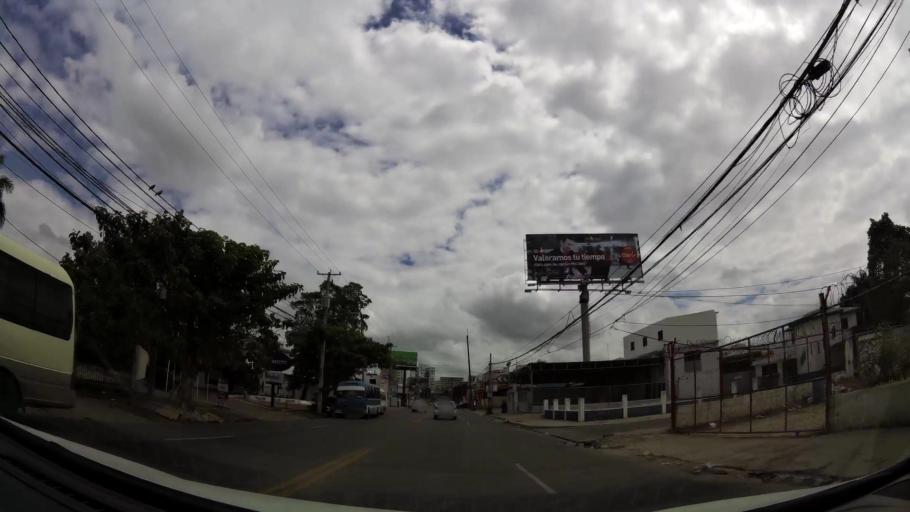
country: DO
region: Nacional
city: La Julia
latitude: 18.4778
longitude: -69.9481
